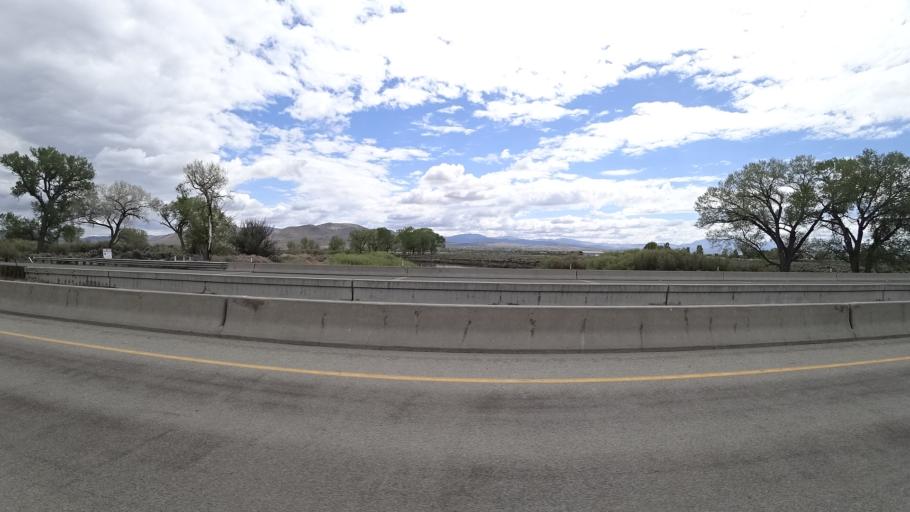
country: US
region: Nevada
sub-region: Douglas County
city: Indian Hills
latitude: 39.0481
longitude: -119.7801
